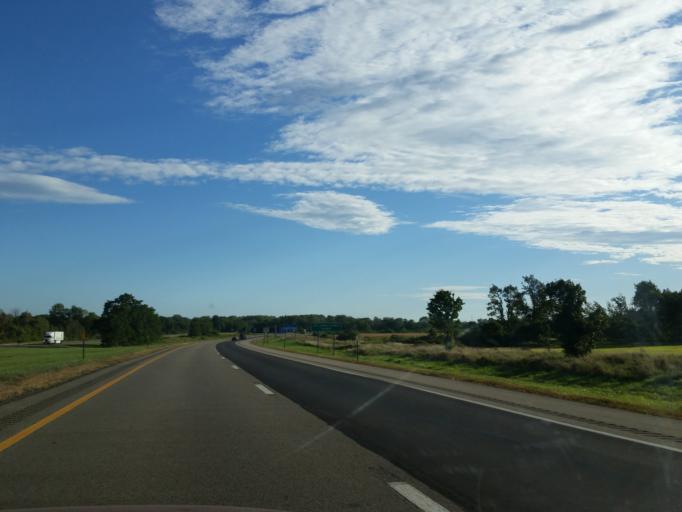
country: US
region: Pennsylvania
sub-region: Erie County
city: North East
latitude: 42.2530
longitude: -79.7610
